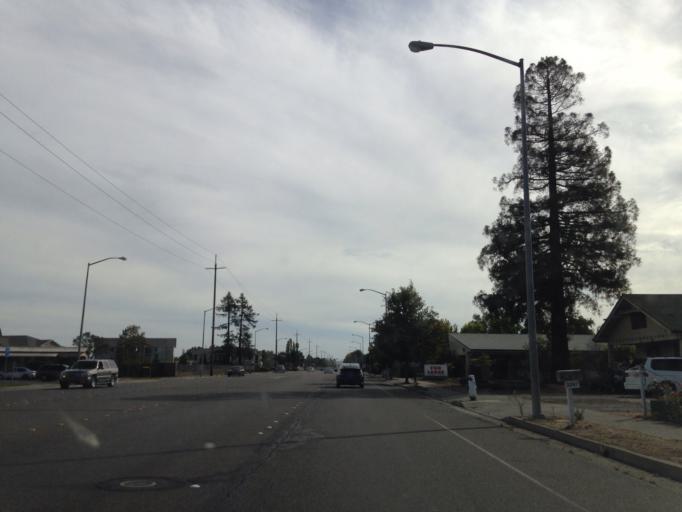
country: US
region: California
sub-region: Sonoma County
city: Roseland
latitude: 38.3981
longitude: -122.7137
